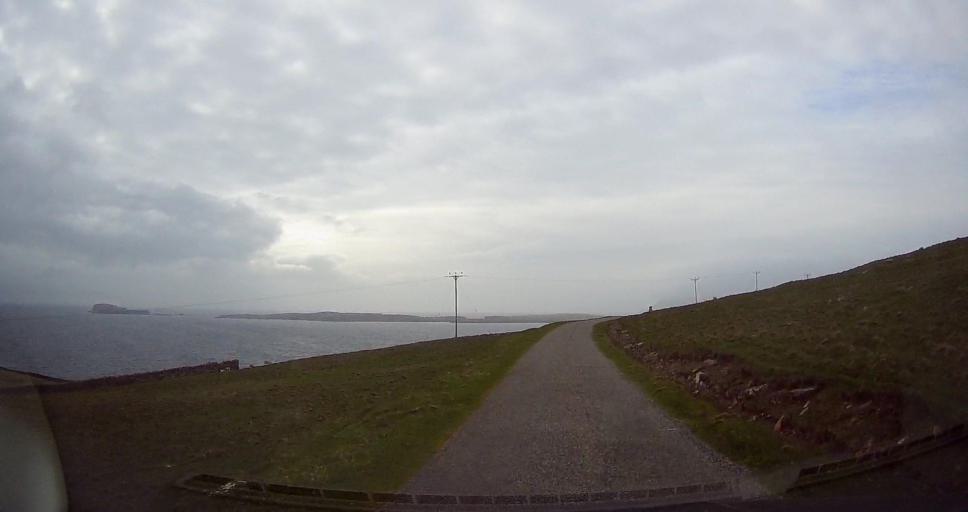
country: GB
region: Scotland
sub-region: Shetland Islands
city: Sandwick
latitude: 59.8584
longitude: -1.2735
